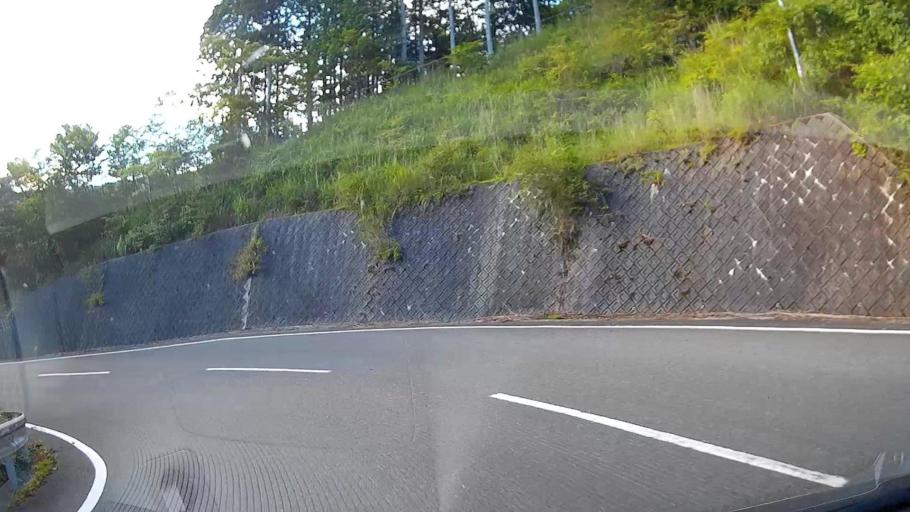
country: JP
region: Shizuoka
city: Shizuoka-shi
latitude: 35.1577
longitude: 138.2645
